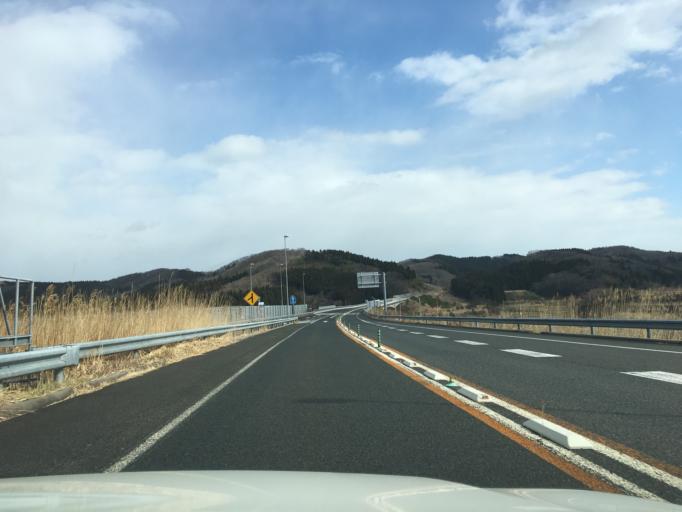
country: JP
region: Akita
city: Akita Shi
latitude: 39.5475
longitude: 140.0734
